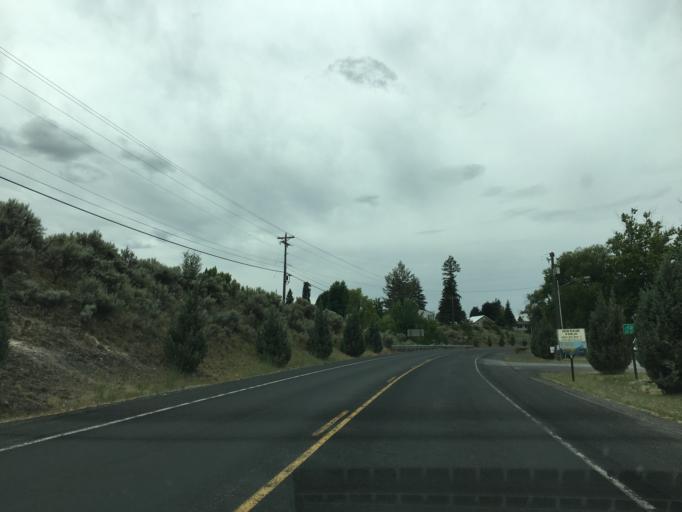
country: US
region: Washington
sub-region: Okanogan County
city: Coulee Dam
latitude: 47.9347
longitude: -119.0271
